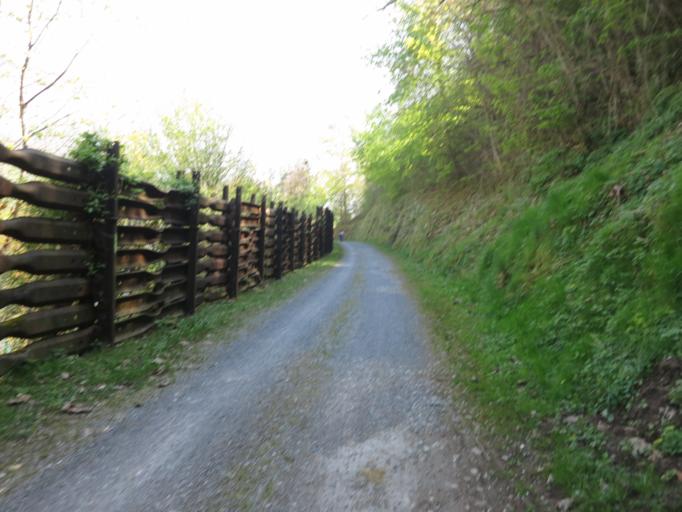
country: CH
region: Saint Gallen
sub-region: Wahlkreis See-Gaster
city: Amden
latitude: 47.1221
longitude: 9.1500
